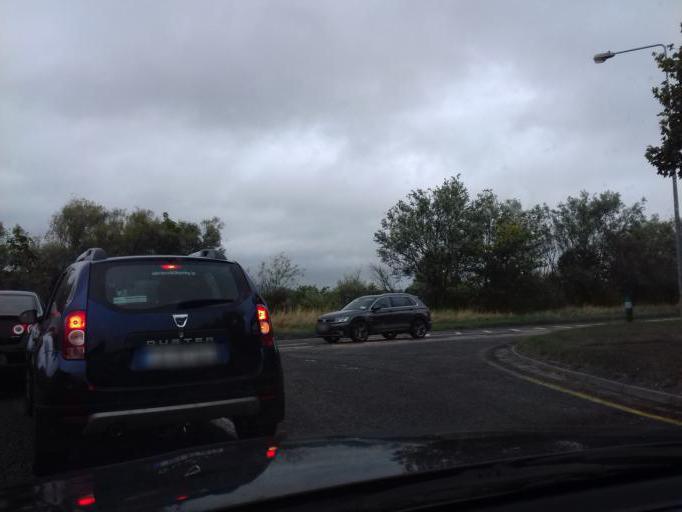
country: IE
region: Leinster
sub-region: County Carlow
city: Bagenalstown
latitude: 52.7449
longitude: -6.9698
